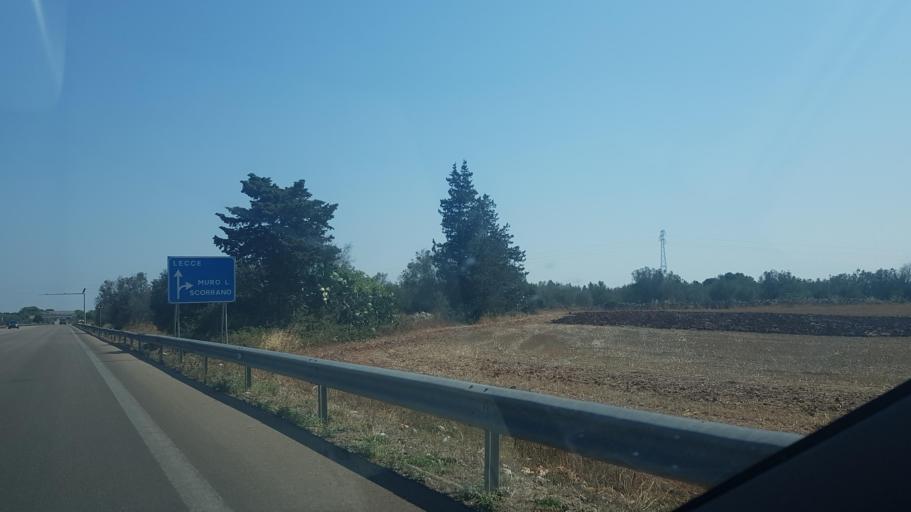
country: IT
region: Apulia
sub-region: Provincia di Lecce
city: Scorrano
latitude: 40.0904
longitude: 18.3110
